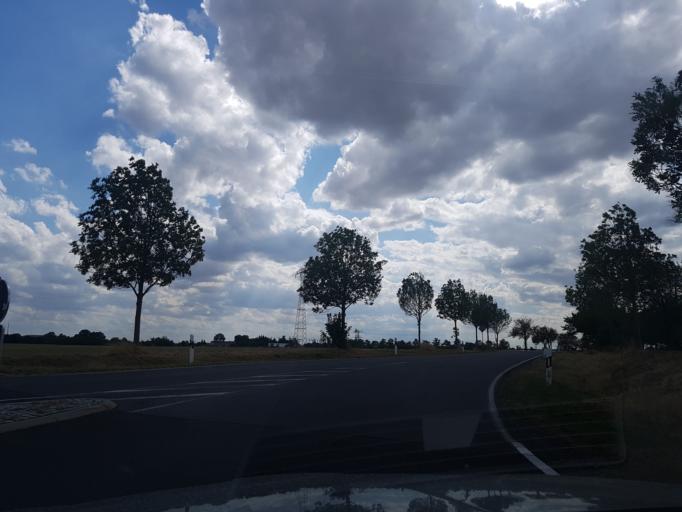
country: DE
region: Saxony
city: Priestewitz
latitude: 51.2406
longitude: 13.5500
